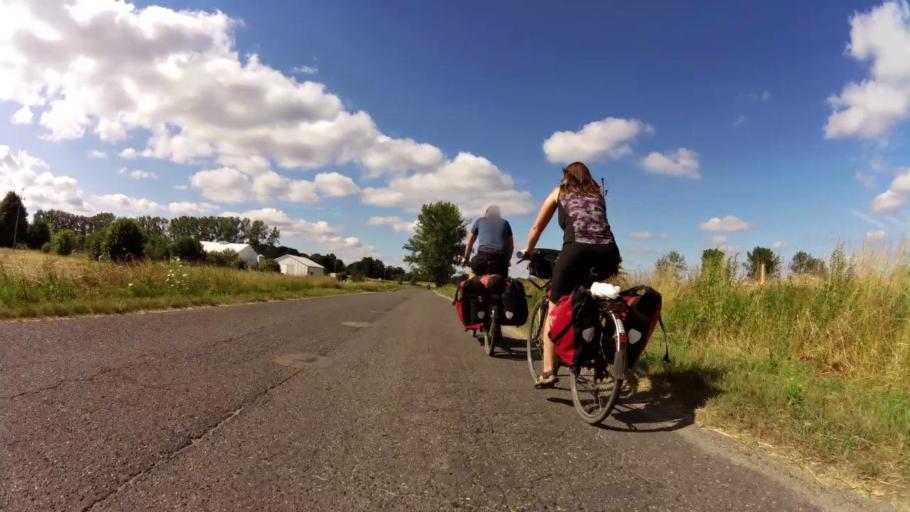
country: PL
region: West Pomeranian Voivodeship
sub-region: Powiat lobeski
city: Lobez
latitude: 53.6356
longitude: 15.6754
